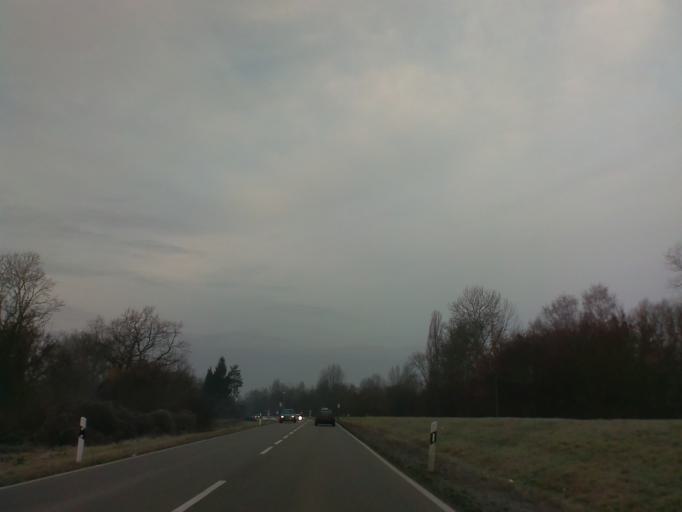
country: DE
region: Rheinland-Pfalz
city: Altrip
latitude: 49.4383
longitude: 8.4695
